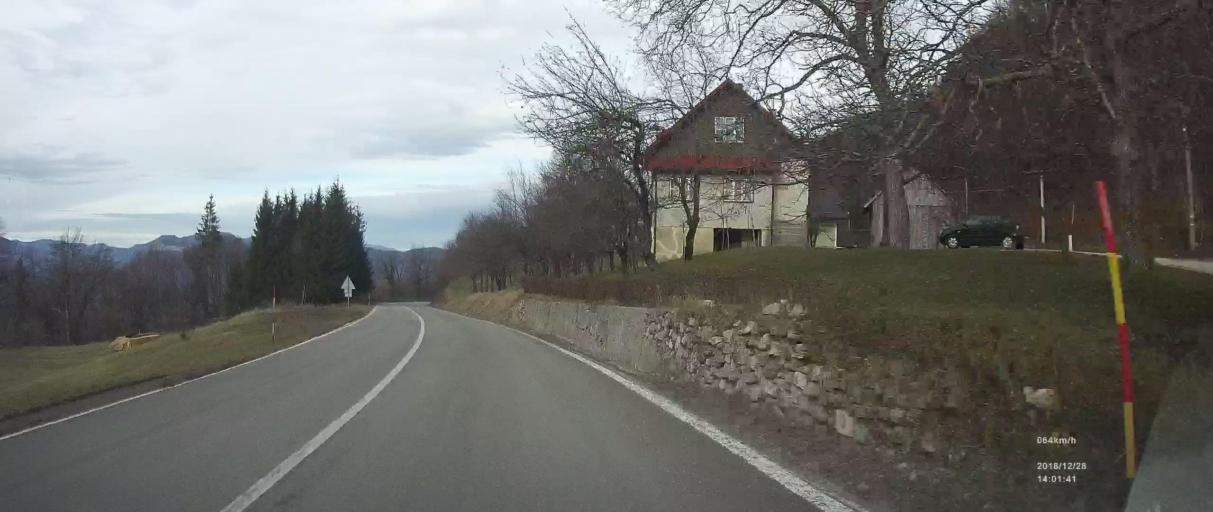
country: SI
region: Kostel
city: Kostel
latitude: 45.4226
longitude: 14.9071
